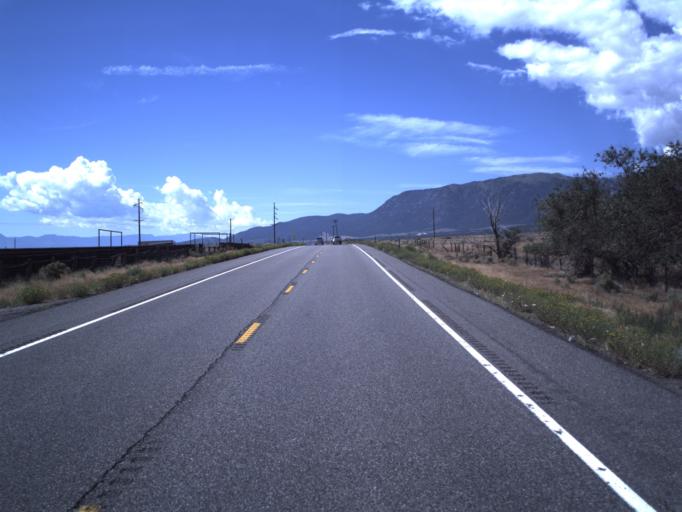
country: US
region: Utah
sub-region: Piute County
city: Junction
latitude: 38.4327
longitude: -112.2313
